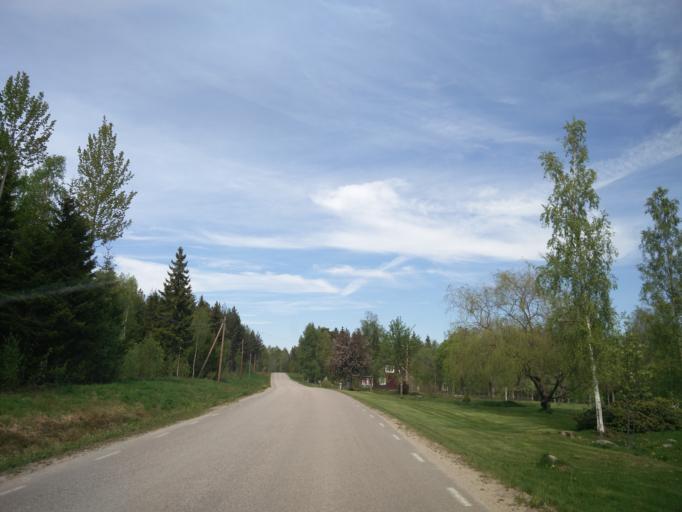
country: SE
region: Gaevleborg
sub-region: Hudiksvalls Kommun
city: Sorforsa
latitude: 61.6834
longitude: 16.9246
